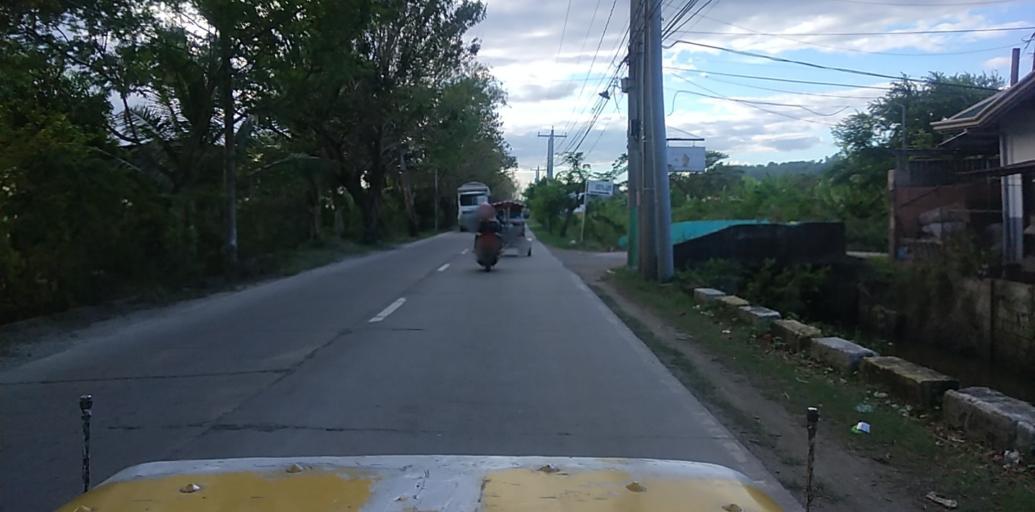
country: PH
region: Central Luzon
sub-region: Province of Pampanga
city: Arayat
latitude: 15.1493
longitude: 120.7561
